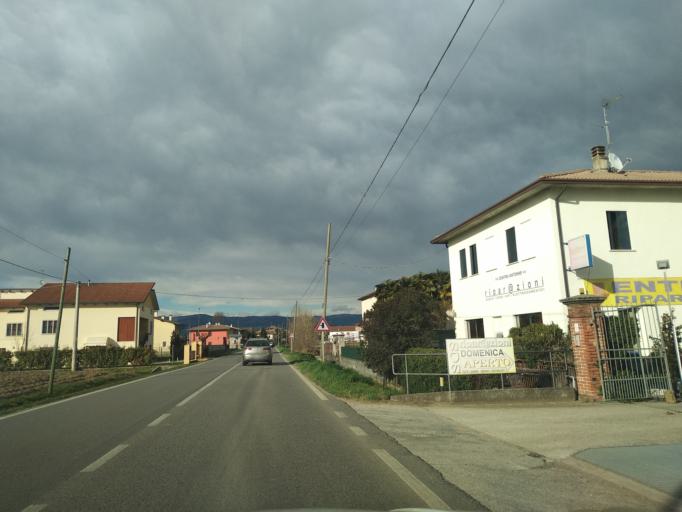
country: IT
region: Veneto
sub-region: Provincia di Vicenza
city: Poianella
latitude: 45.6273
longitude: 11.6232
